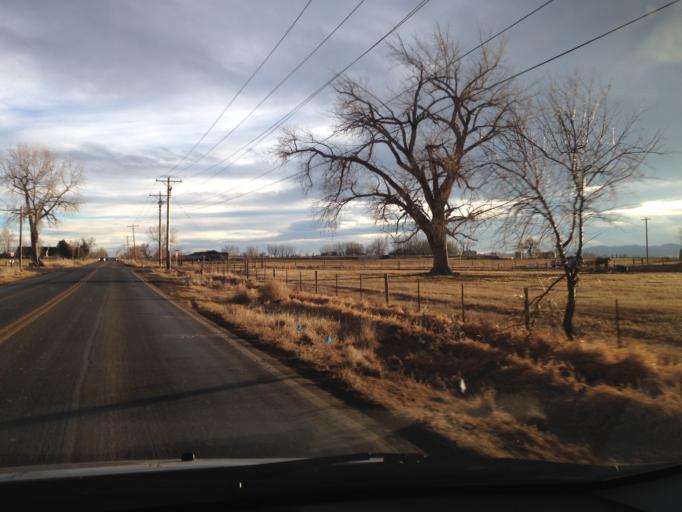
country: US
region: Colorado
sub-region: Weld County
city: Firestone
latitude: 40.1179
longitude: -104.9989
